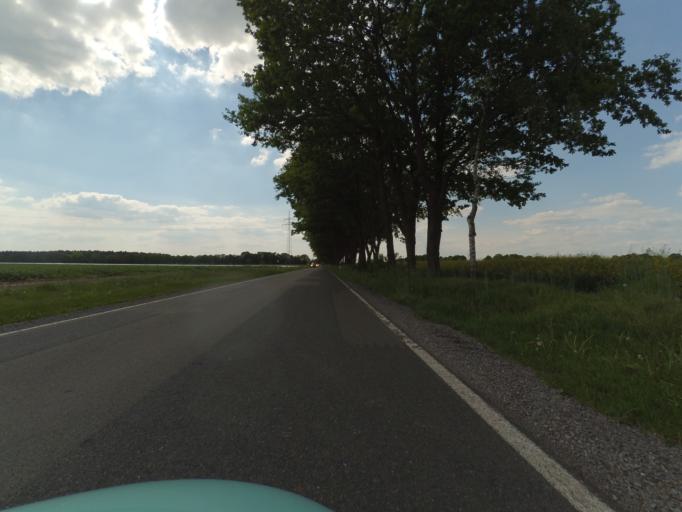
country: DE
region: Lower Saxony
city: Dollbergen
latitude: 52.4508
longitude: 10.1500
